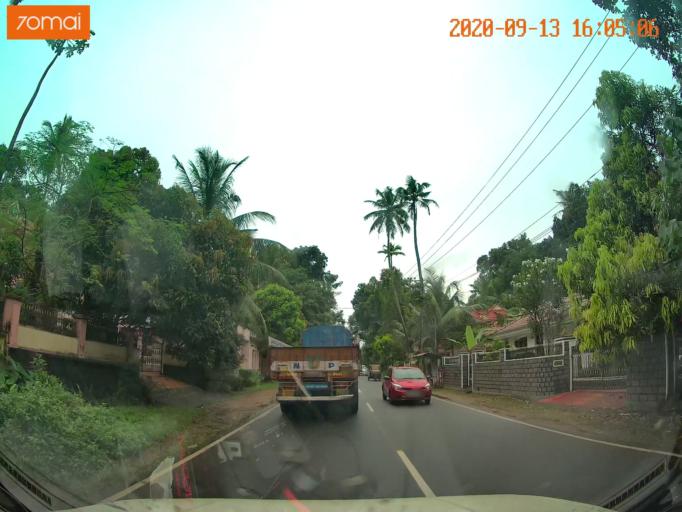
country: IN
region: Kerala
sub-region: Kottayam
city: Palackattumala
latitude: 9.6691
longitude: 76.5737
